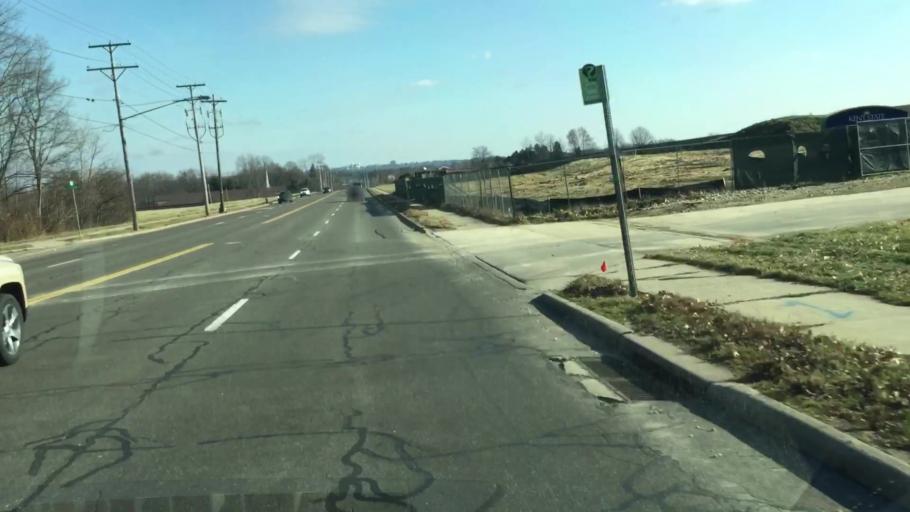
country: US
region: Ohio
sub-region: Summit County
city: Stow
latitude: 41.1581
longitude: -81.4165
